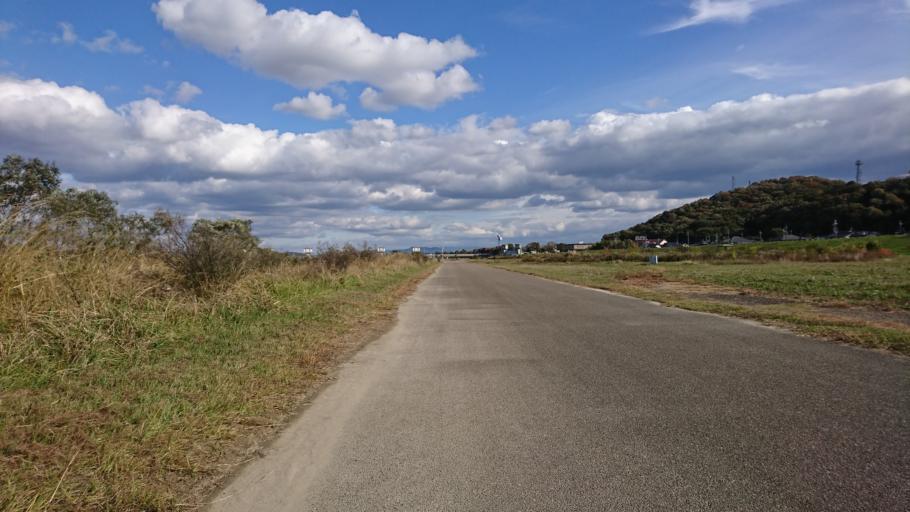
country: JP
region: Hyogo
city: Kakogawacho-honmachi
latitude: 34.7940
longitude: 134.8813
